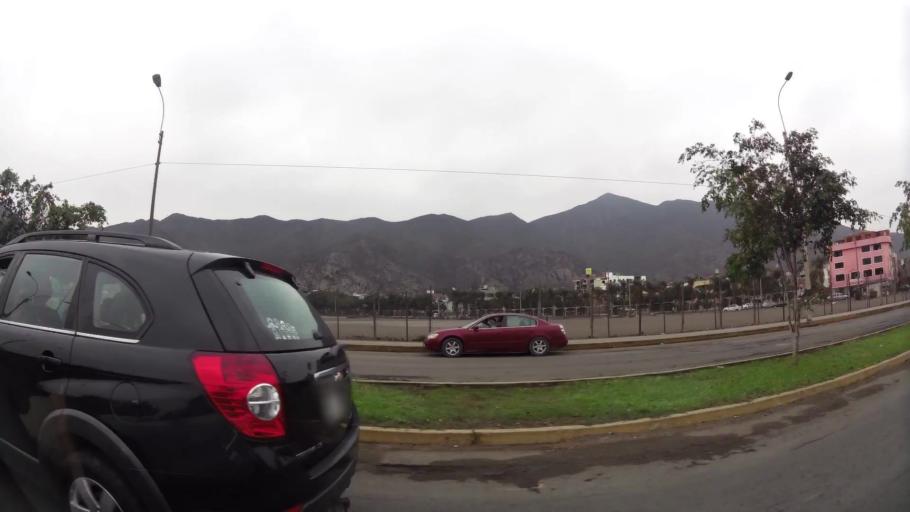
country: PE
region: Lima
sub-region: Lima
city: La Molina
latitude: -12.0597
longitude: -76.9381
